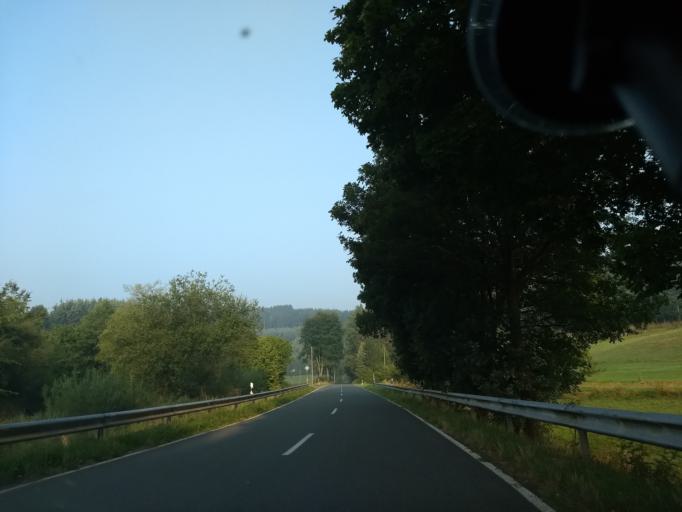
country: DE
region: North Rhine-Westphalia
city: Eslohe
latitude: 51.2352
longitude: 8.0838
